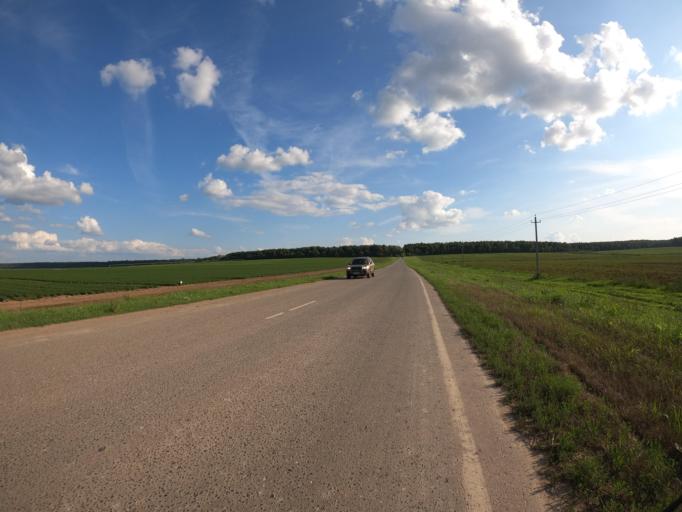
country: RU
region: Moskovskaya
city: Meshcherino
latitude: 55.1873
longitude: 38.4719
